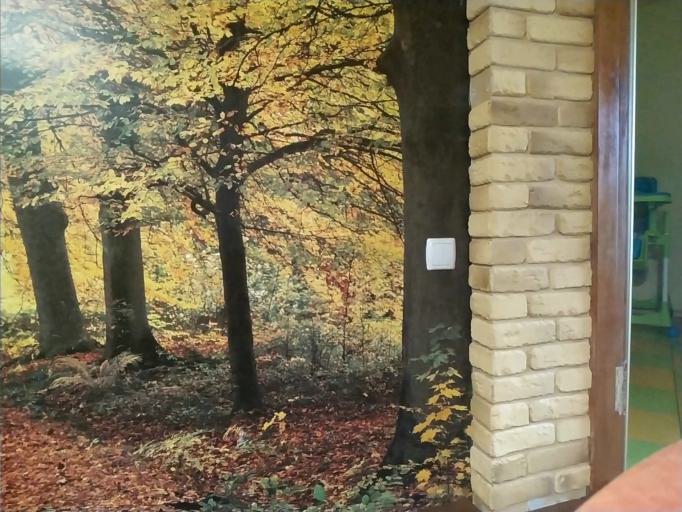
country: RU
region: Tverskaya
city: Likhoslavl'
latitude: 56.9375
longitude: 35.6296
